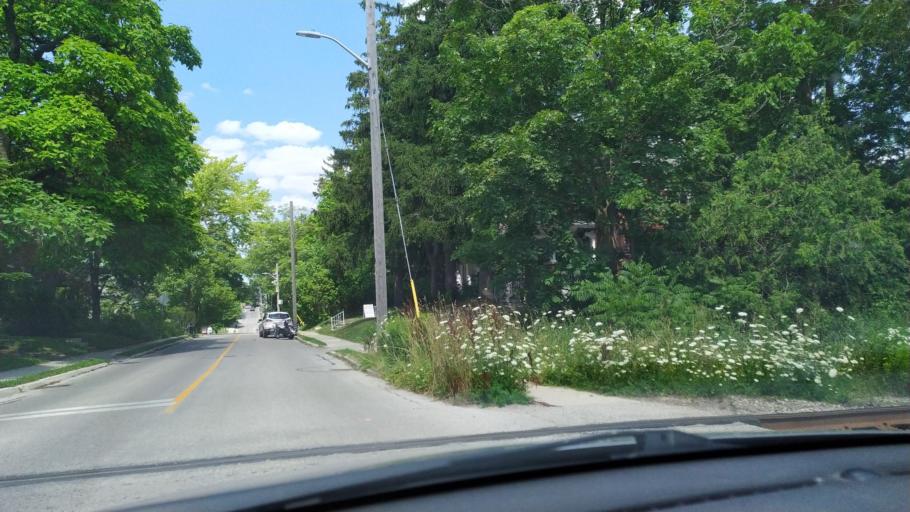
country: CA
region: Ontario
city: Stratford
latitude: 43.3685
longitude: -80.9880
